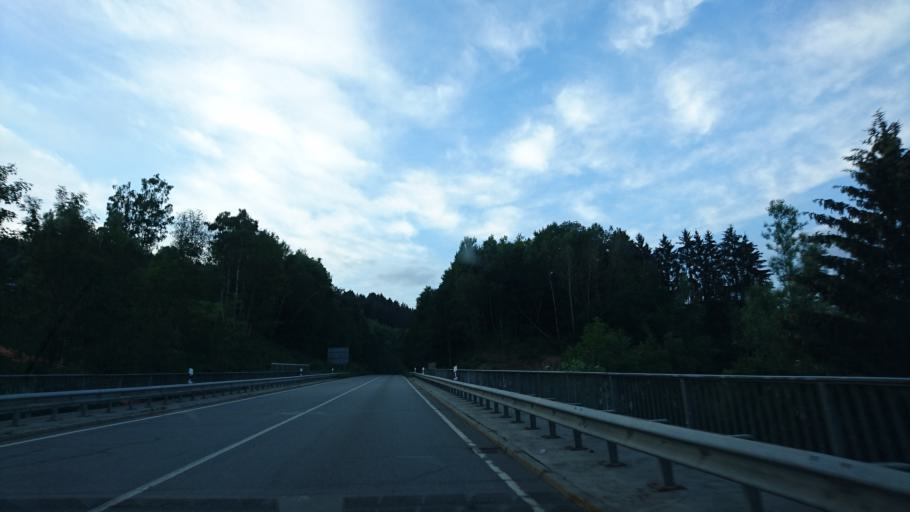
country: DE
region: Bavaria
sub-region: Lower Bavaria
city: Grafenau
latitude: 48.8575
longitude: 13.3850
